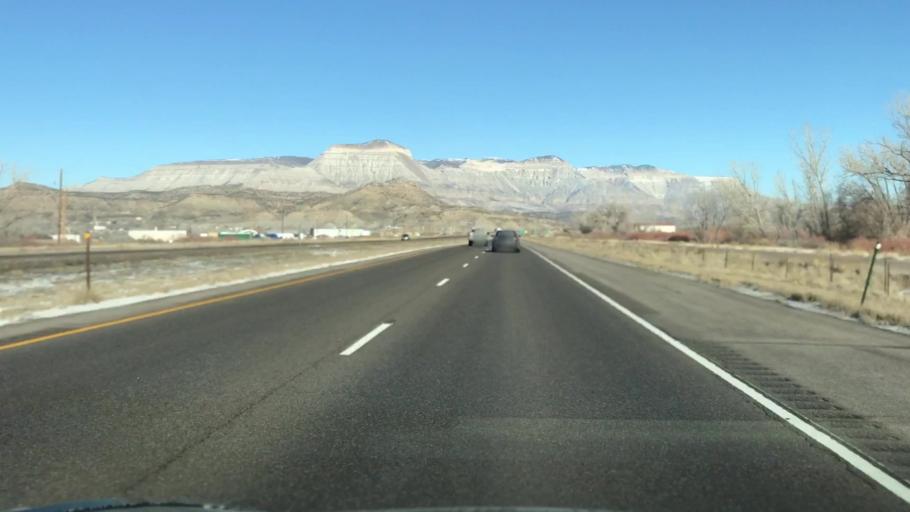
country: US
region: Colorado
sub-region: Garfield County
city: Parachute
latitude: 39.3150
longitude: -108.2126
